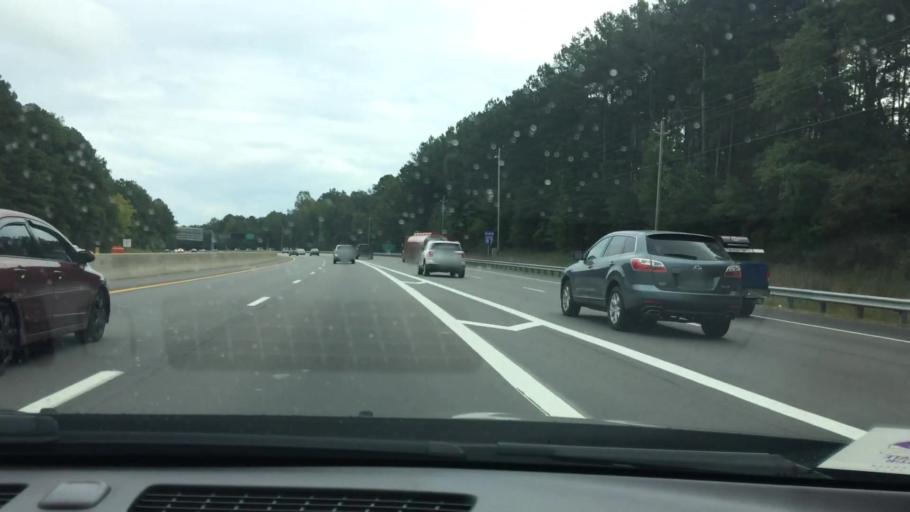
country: US
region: North Carolina
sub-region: Wake County
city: Garner
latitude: 35.7533
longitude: -78.5876
